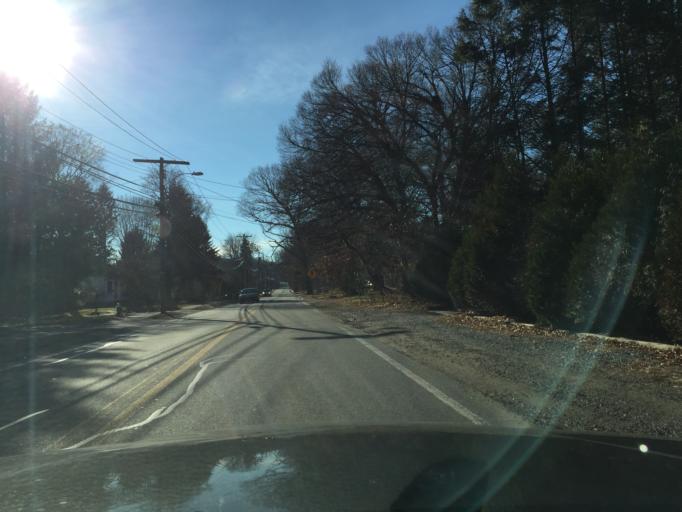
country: US
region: Massachusetts
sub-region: Middlesex County
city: Lexington
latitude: 42.4420
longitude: -71.2006
